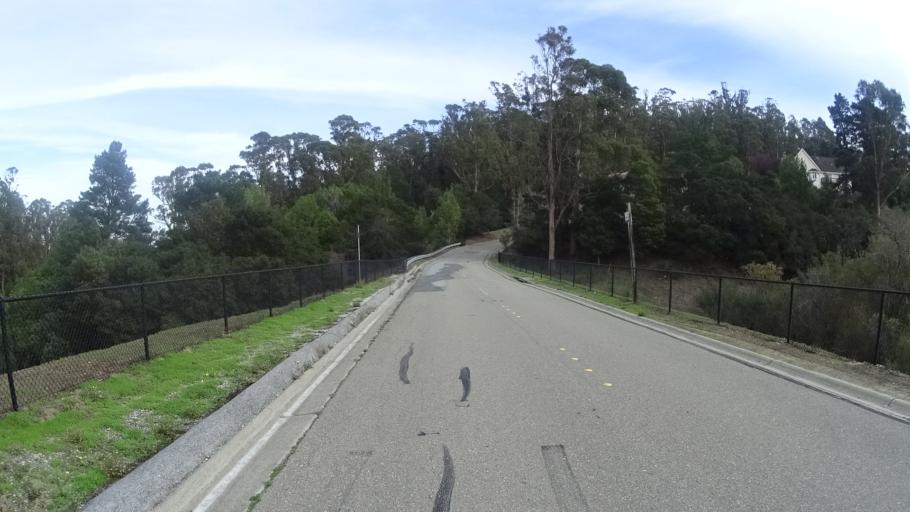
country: US
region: California
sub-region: San Mateo County
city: Hillsborough
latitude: 37.5704
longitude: -122.3798
